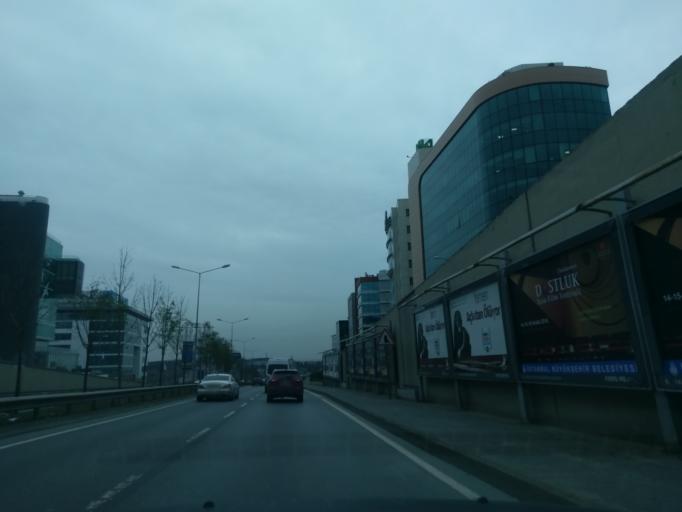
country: TR
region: Istanbul
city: Umraniye
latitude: 41.0936
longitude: 29.0957
